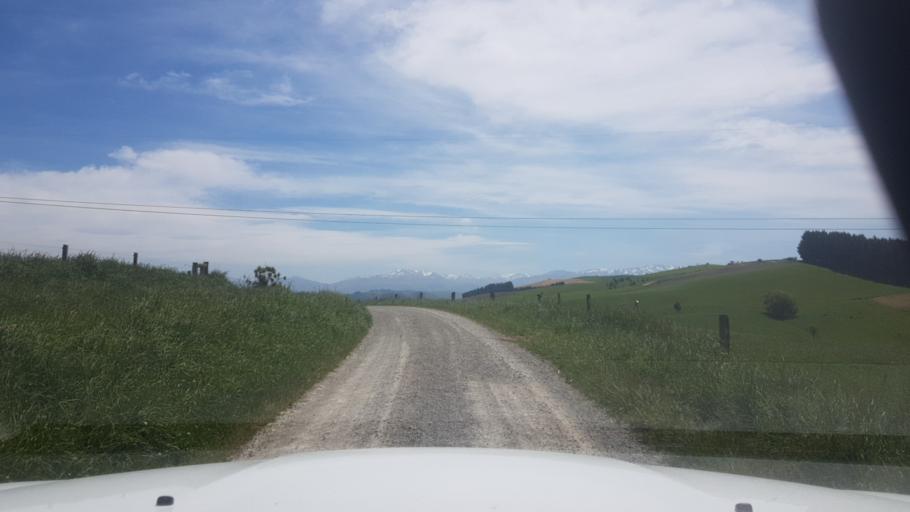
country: NZ
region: Canterbury
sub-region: Timaru District
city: Pleasant Point
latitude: -44.1314
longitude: 171.0202
